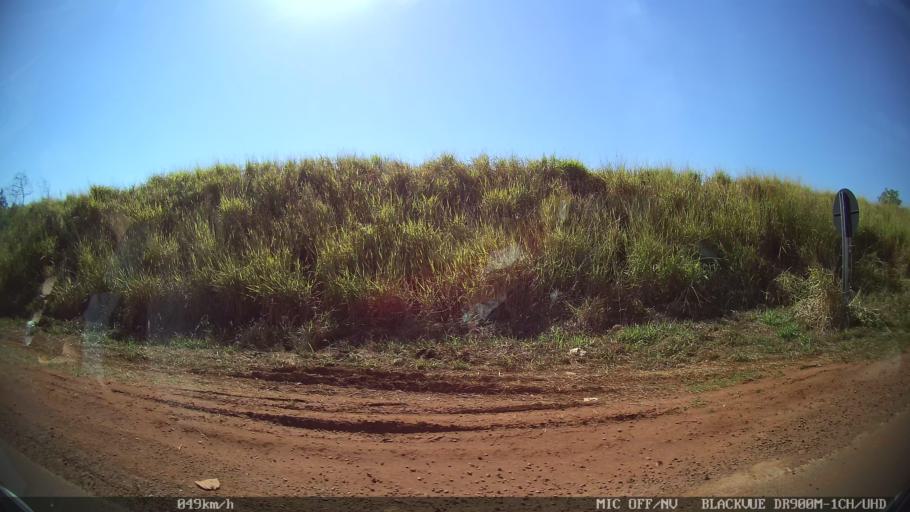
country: BR
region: Sao Paulo
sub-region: Batatais
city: Batatais
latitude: -20.8772
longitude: -47.6051
